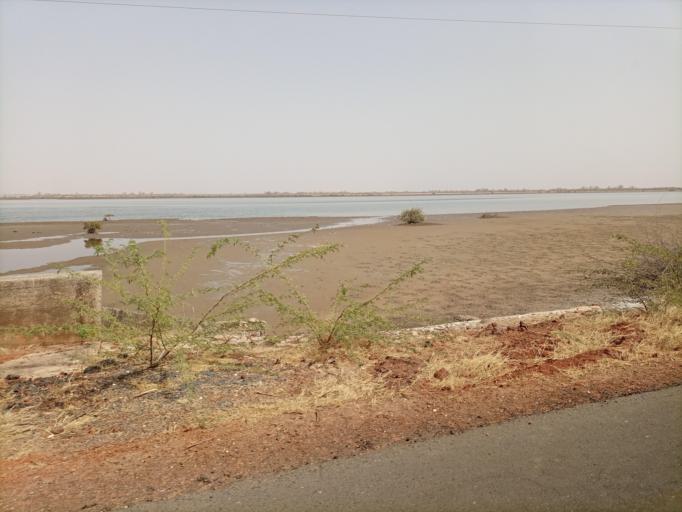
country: SN
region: Fatick
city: Foundiougne
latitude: 14.1901
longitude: -16.4532
